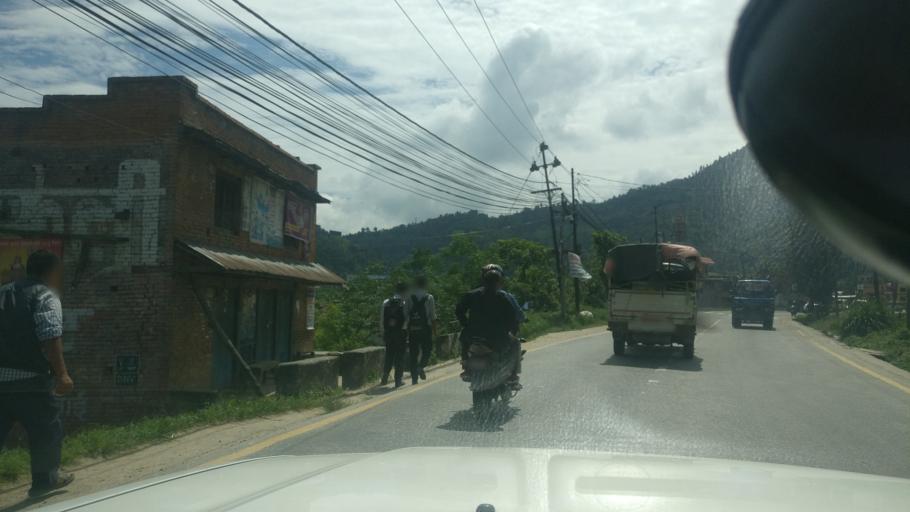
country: NP
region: Central Region
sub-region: Bagmati Zone
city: Hari Bdr Tamang House
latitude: 27.6516
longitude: 85.4620
